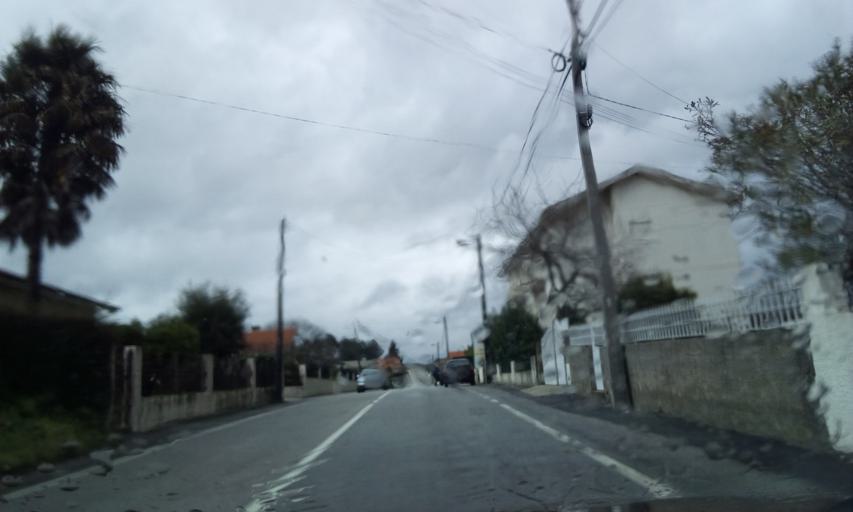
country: PT
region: Viseu
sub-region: Viseu
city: Rio de Loba
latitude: 40.6373
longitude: -7.8664
